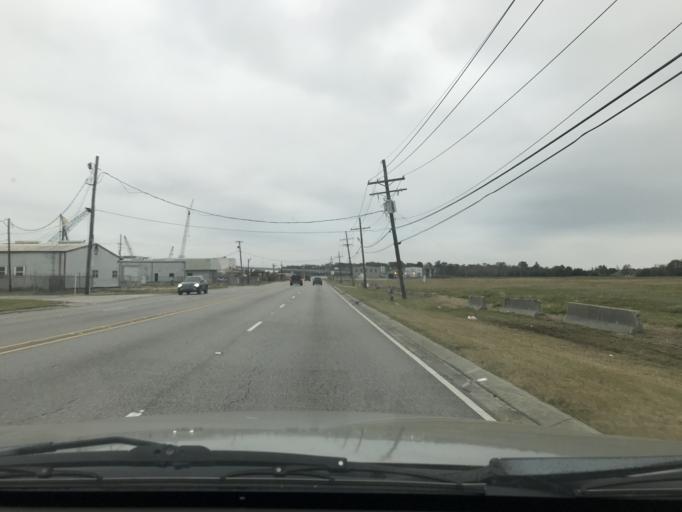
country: US
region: Louisiana
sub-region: Jefferson Parish
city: Woodmere
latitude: 29.8769
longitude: -90.0742
